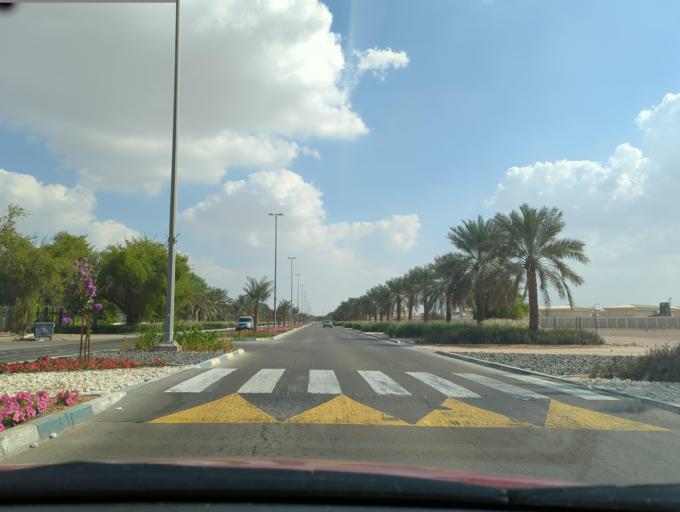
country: AE
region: Abu Dhabi
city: Al Ain
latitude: 24.1841
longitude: 55.6399
